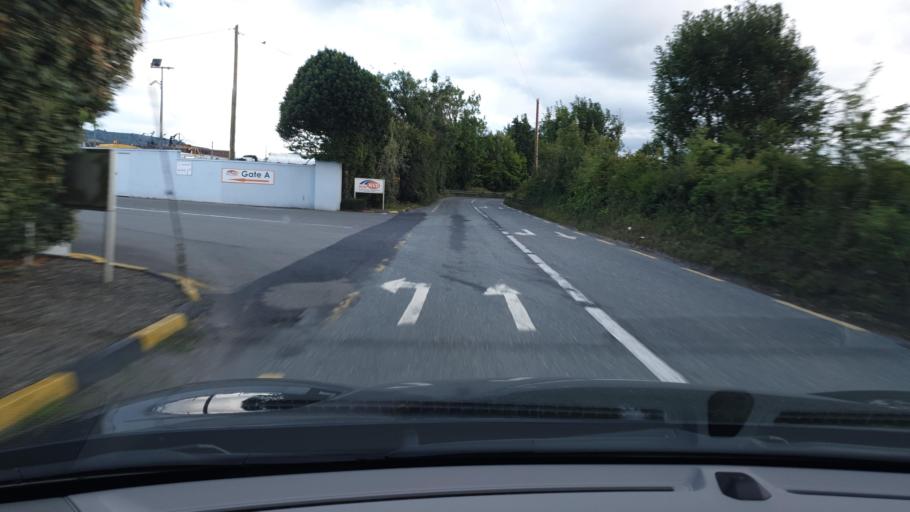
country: IE
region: Leinster
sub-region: South Dublin
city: Saggart
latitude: 53.3003
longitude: -6.4363
